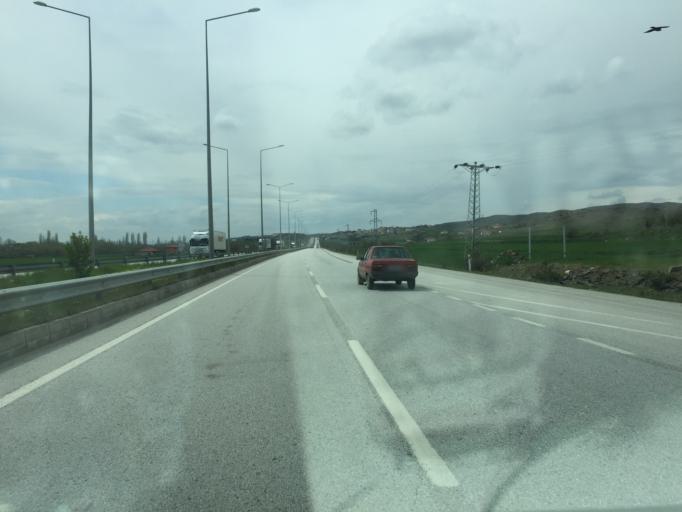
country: TR
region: Corum
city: Sungurlu
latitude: 40.1773
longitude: 34.4420
